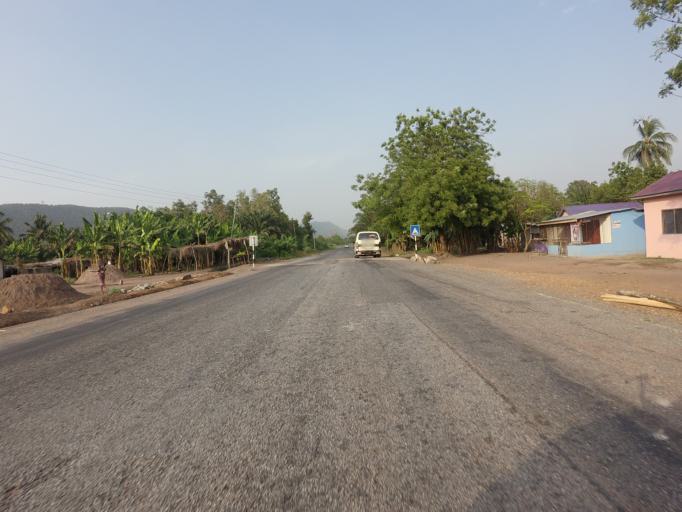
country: GH
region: Volta
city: Ho
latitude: 6.4326
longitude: 0.1911
